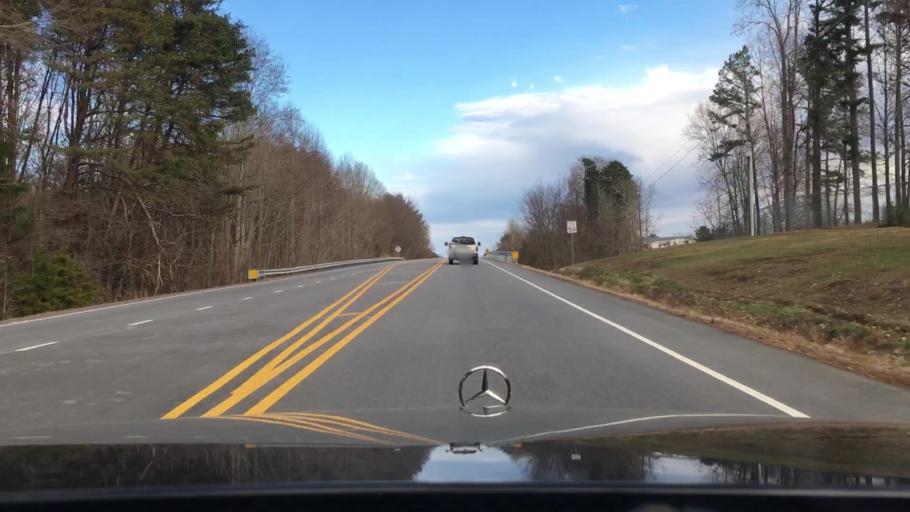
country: US
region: North Carolina
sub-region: Caswell County
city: Yanceyville
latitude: 36.4078
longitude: -79.3334
